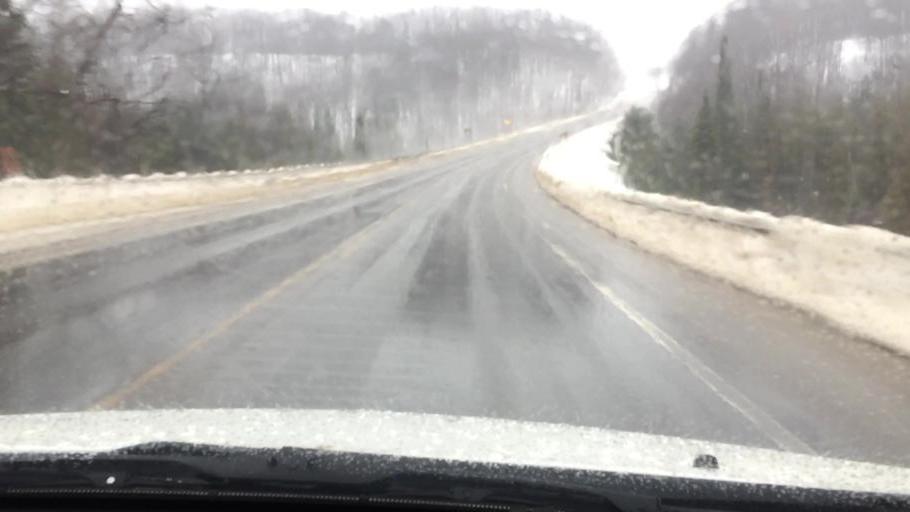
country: US
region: Michigan
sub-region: Antrim County
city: Mancelona
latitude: 44.9569
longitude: -85.0505
